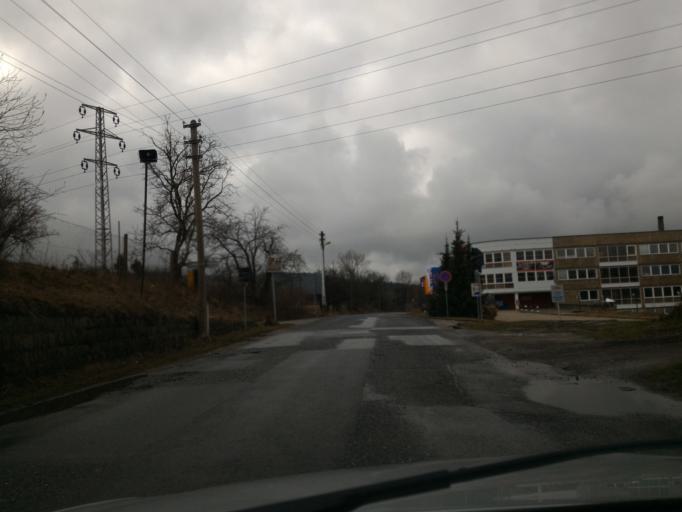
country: CZ
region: Liberecky
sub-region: Okres Liberec
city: Frydlant
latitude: 50.9178
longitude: 15.0609
